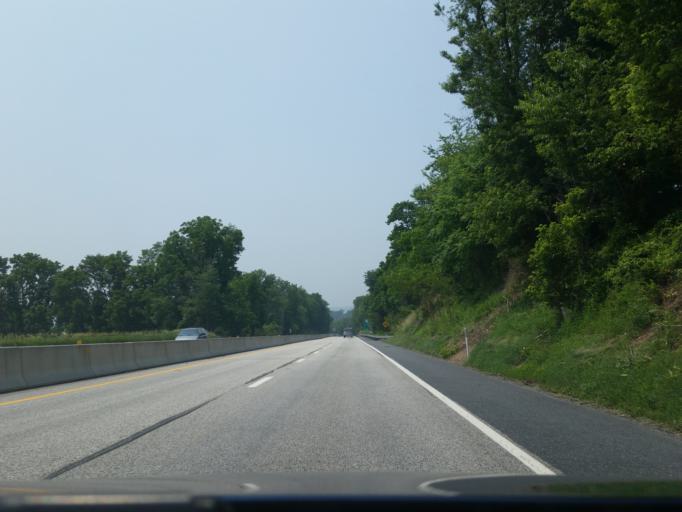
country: US
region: Pennsylvania
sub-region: Lebanon County
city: Jonestown
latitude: 40.4076
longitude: -76.5676
